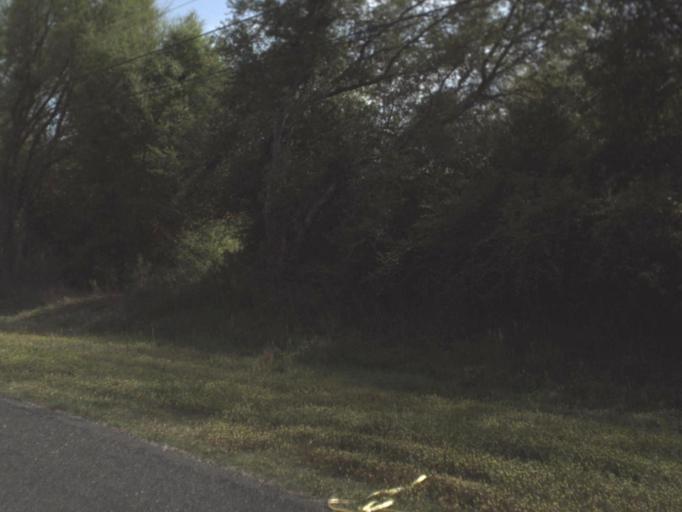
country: US
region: Florida
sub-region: Santa Rosa County
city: East Milton
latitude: 30.6092
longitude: -86.9546
